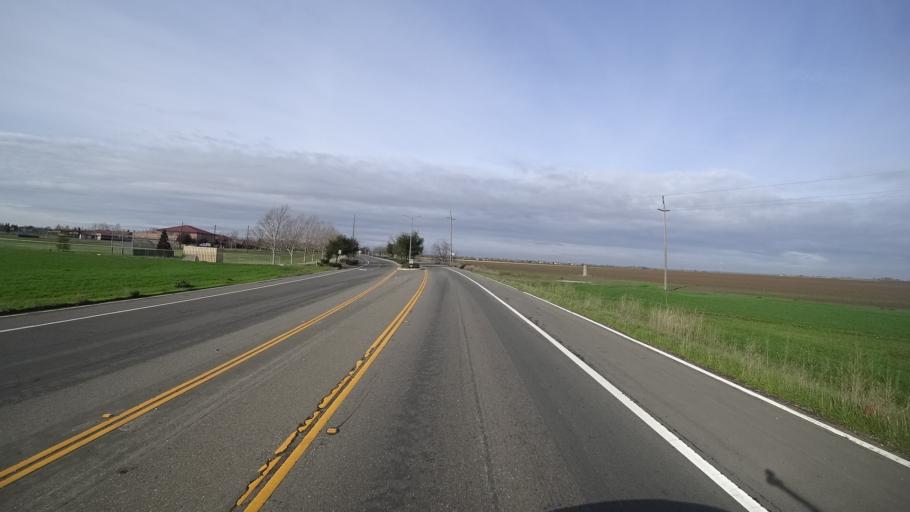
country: US
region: California
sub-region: Yolo County
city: Davis
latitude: 38.5651
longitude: -121.6983
